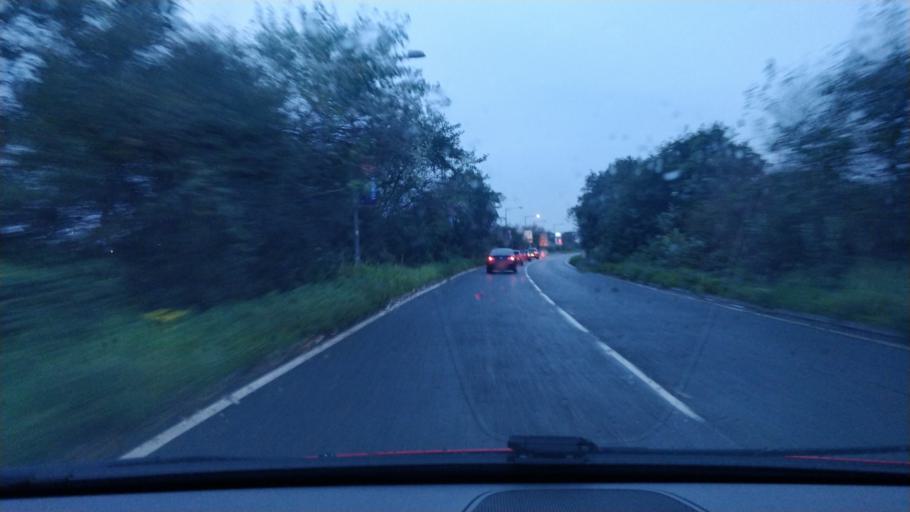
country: GB
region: England
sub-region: Blackpool
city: Blackpool
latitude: 53.7946
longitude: -3.0448
